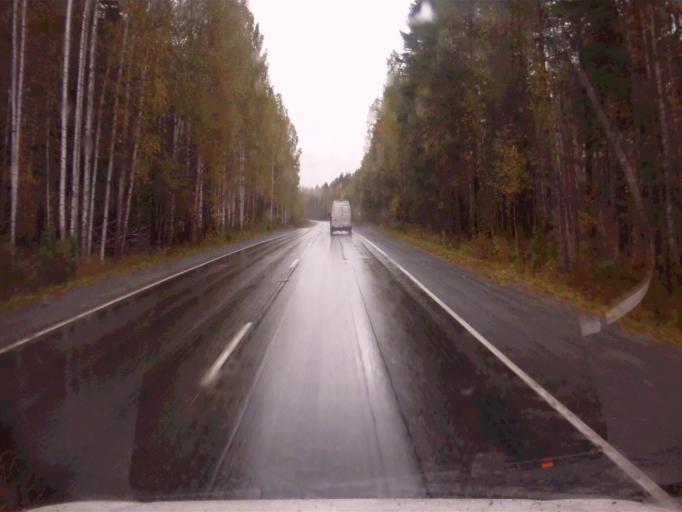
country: RU
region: Chelyabinsk
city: Tayginka
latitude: 55.5659
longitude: 60.6499
